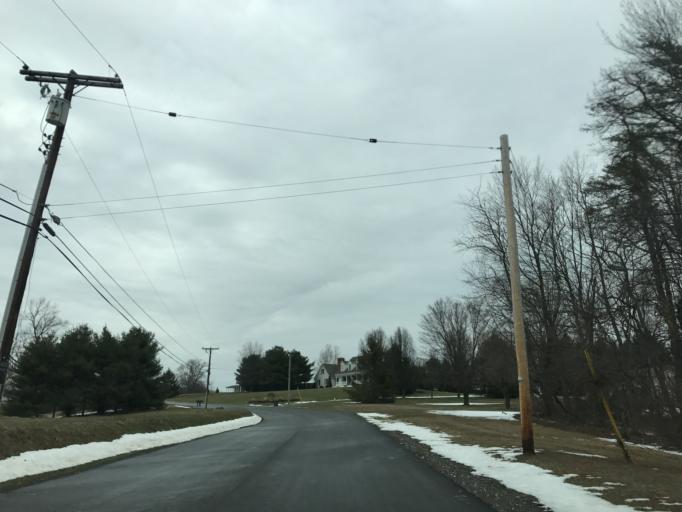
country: US
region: Pennsylvania
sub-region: York County
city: New Freedom
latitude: 39.6262
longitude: -76.7034
